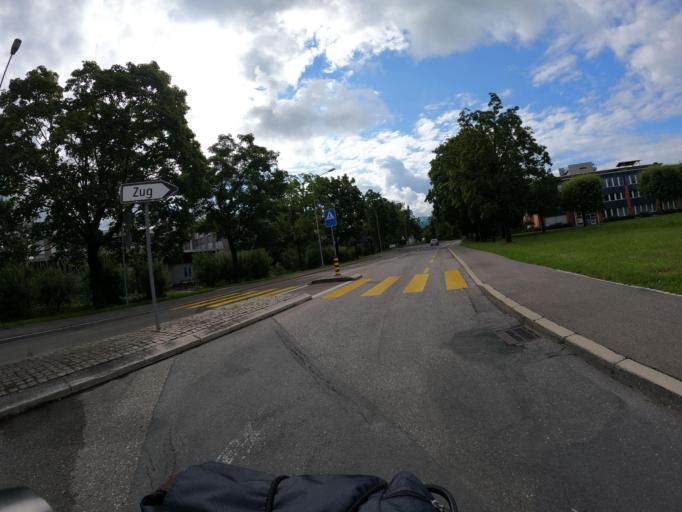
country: CH
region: Zug
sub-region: Zug
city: Steinhausen
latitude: 47.1865
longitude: 8.4935
